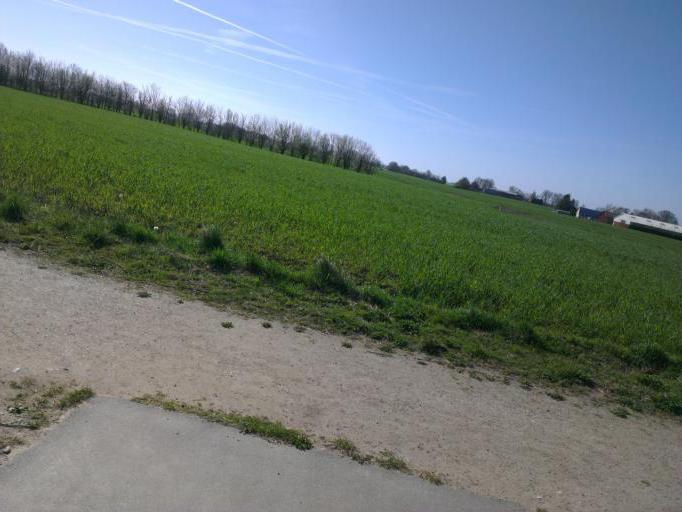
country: DK
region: Capital Region
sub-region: Frederikssund Kommune
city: Frederikssund
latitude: 55.8155
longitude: 12.0735
